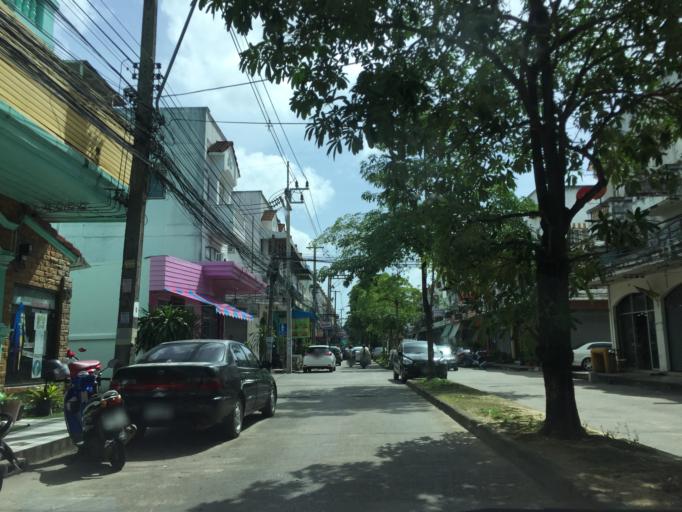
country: TH
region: Phuket
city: Wichit
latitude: 7.9058
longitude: 98.3772
